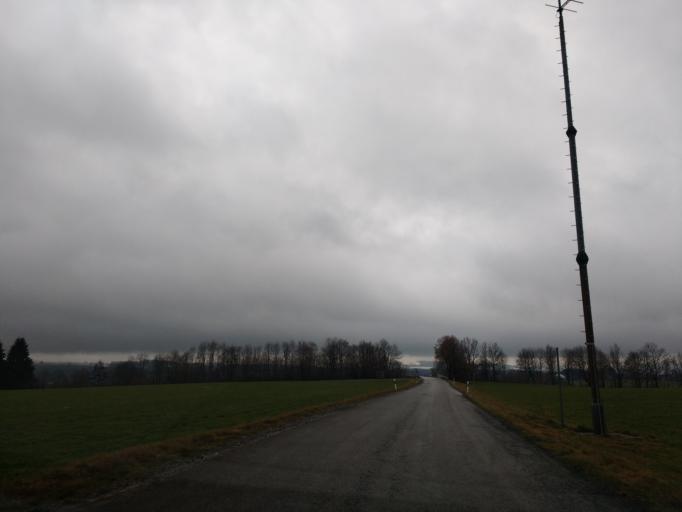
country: DE
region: Bavaria
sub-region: Swabia
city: Neuburg
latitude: 47.7447
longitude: 10.3514
